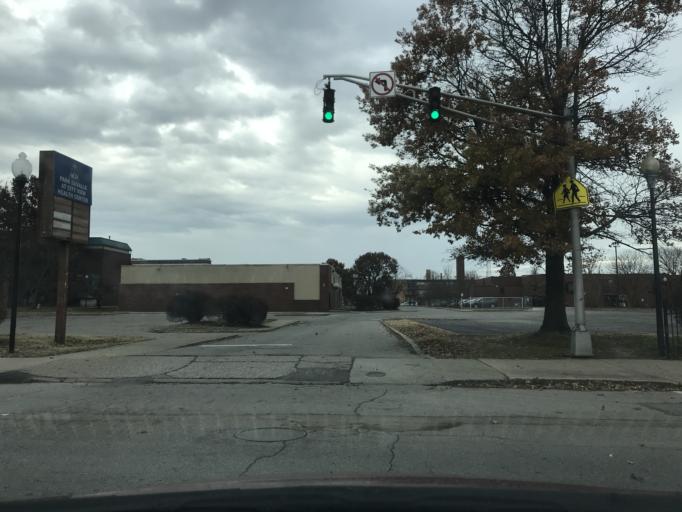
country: US
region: Kentucky
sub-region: Jefferson County
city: Louisville
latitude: 38.2525
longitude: -85.7691
